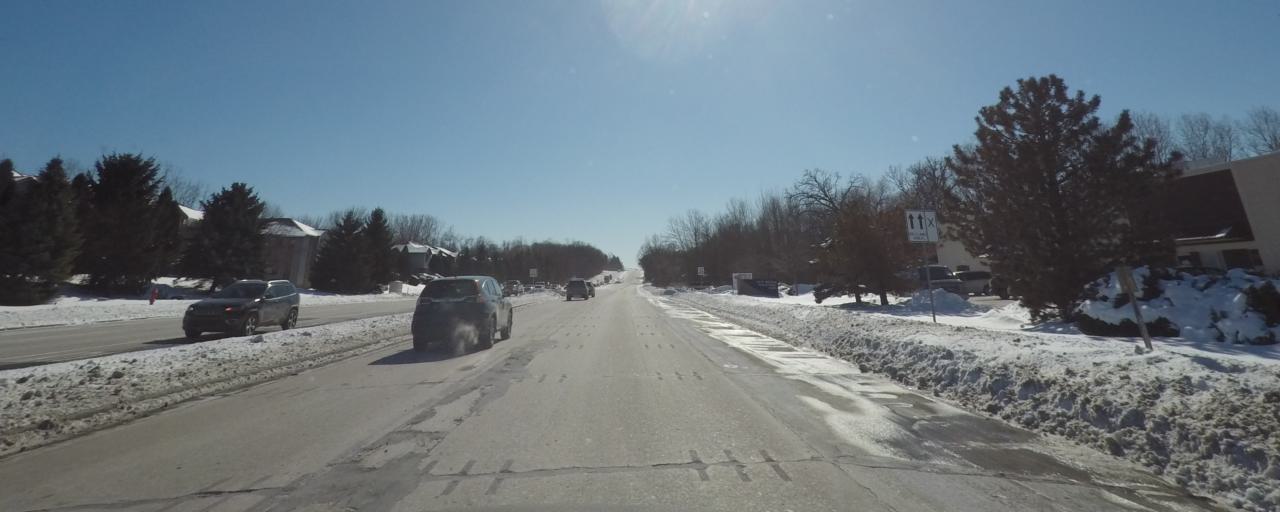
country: US
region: Wisconsin
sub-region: Waukesha County
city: New Berlin
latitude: 42.9908
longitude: -88.1084
